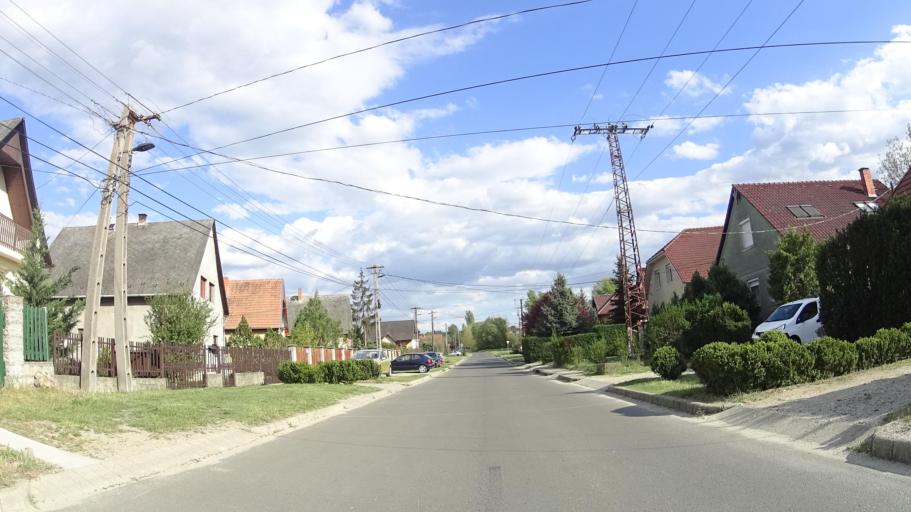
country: HU
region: Pest
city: Veresegyhaz
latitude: 47.6480
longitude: 19.2991
